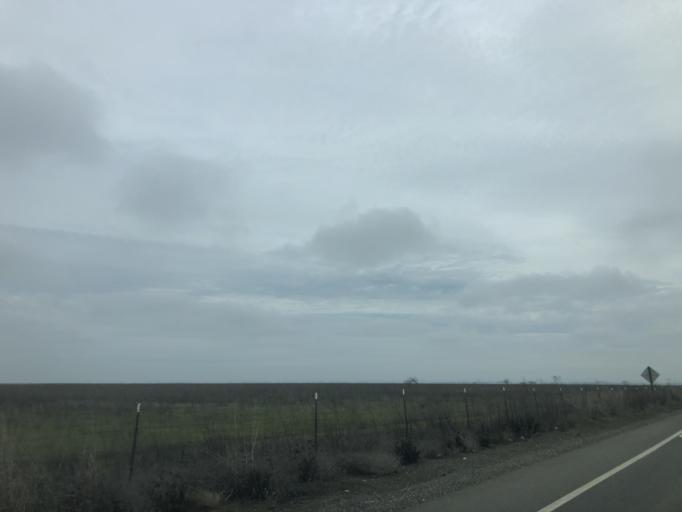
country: US
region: California
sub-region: Sacramento County
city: Elverta
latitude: 38.7144
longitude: -121.5755
